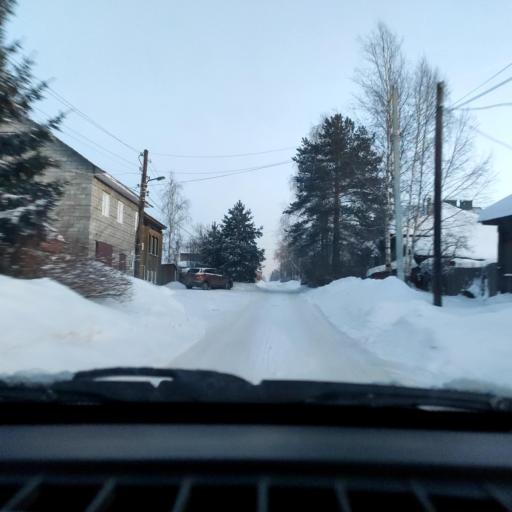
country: RU
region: Perm
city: Perm
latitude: 58.0414
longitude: 56.3382
